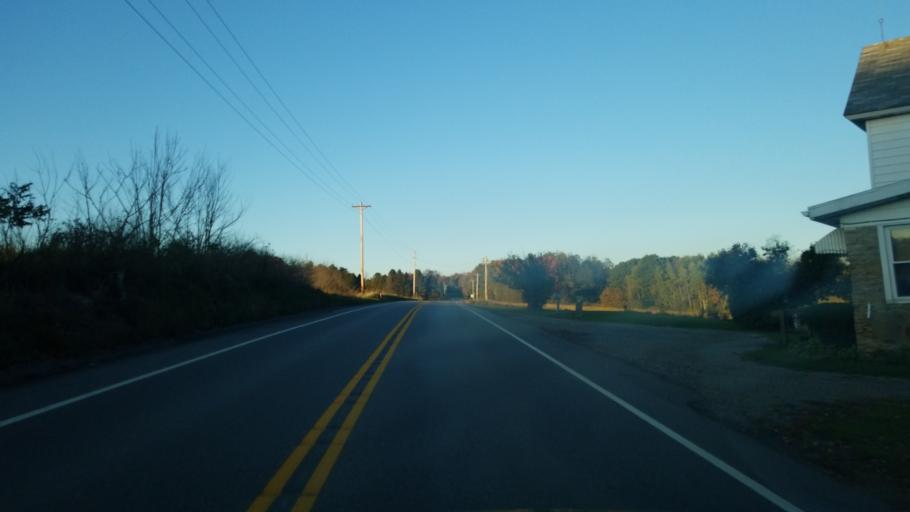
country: US
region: Pennsylvania
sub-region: Jefferson County
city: Reynoldsville
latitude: 41.0512
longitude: -78.9359
